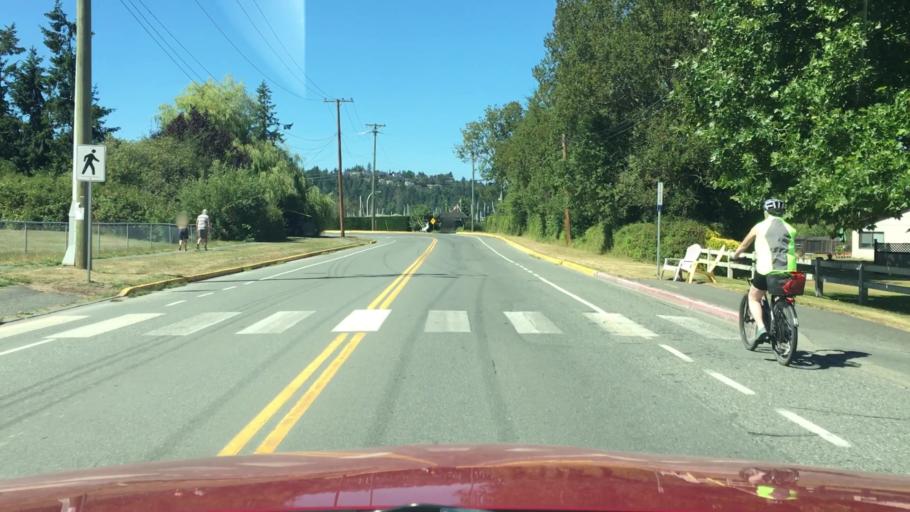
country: CA
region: British Columbia
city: North Saanich
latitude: 48.6694
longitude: -123.4177
